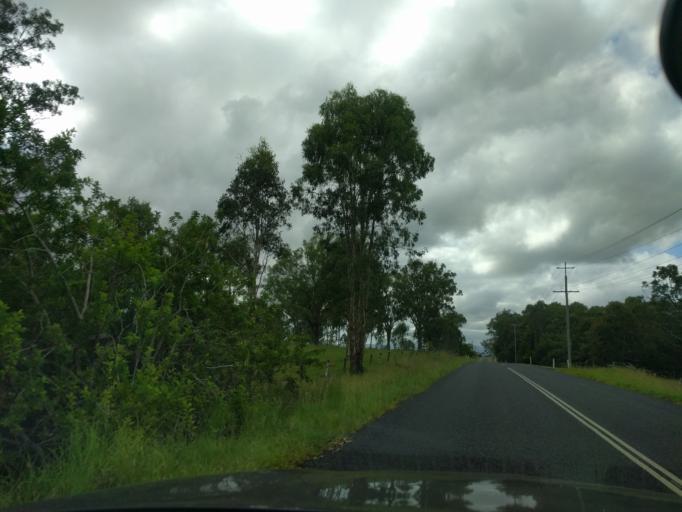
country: AU
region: Queensland
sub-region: Logan
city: Cedar Vale
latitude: -28.0022
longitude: 152.9892
